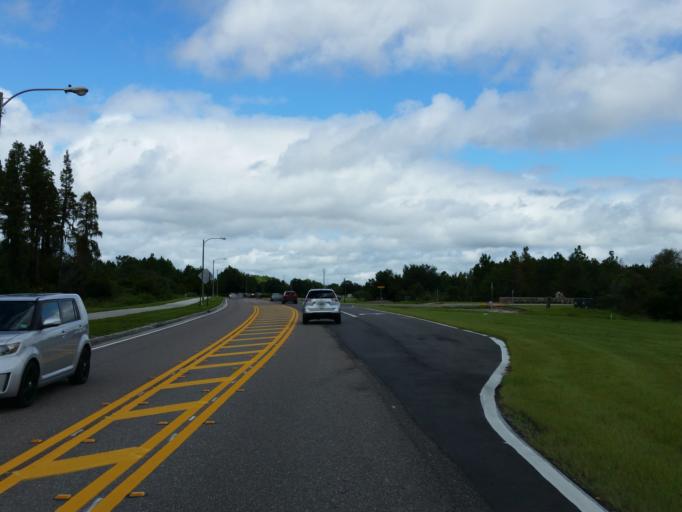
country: US
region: Florida
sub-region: Pasco County
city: Wesley Chapel
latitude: 28.2027
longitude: -82.2995
